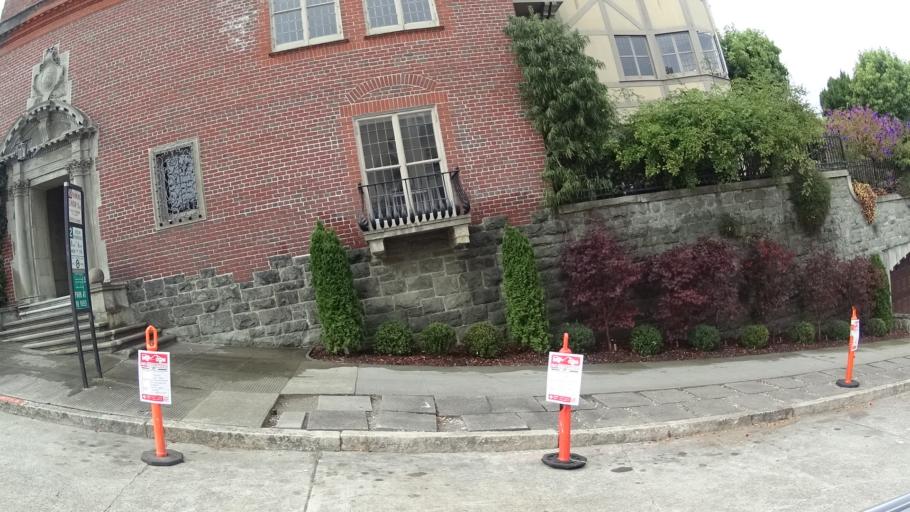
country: US
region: California
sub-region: San Francisco County
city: San Francisco
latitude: 37.7923
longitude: -122.4379
